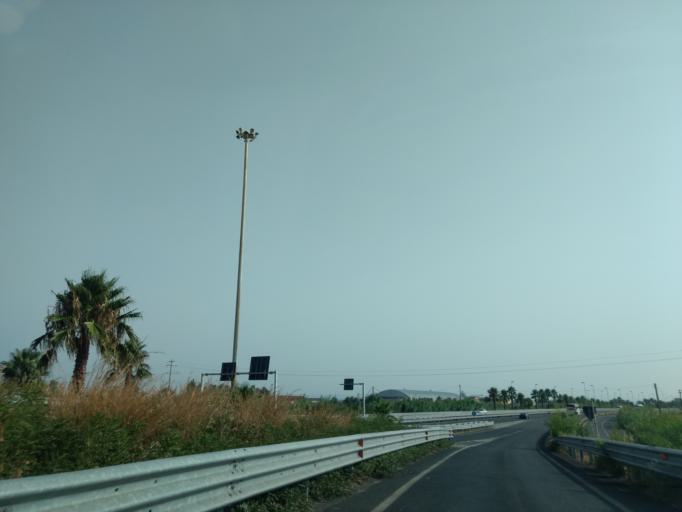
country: IT
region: Sicily
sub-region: Catania
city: Catania
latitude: 37.4775
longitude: 15.0610
